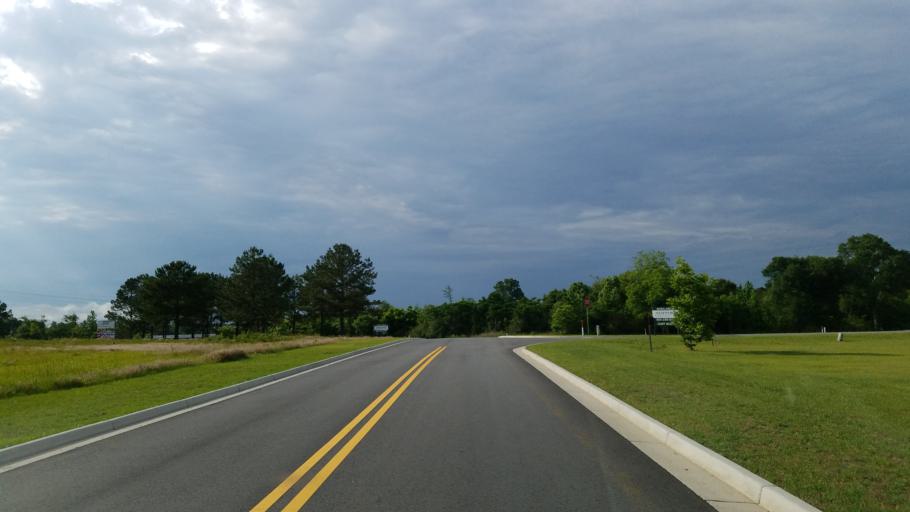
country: US
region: Georgia
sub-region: Tift County
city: Tifton
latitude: 31.4460
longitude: -83.5451
